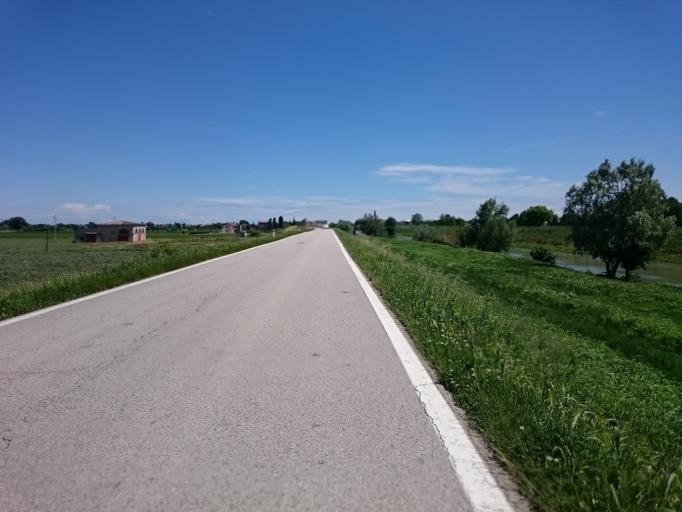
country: IT
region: Veneto
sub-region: Provincia di Padova
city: Pontelongo
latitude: 45.2533
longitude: 12.0058
